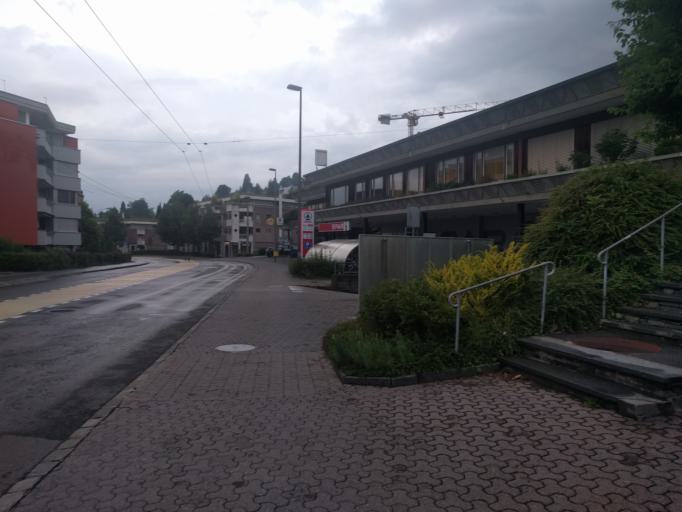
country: CH
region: Lucerne
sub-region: Lucerne-Land District
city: Adligenswil
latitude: 47.0548
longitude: 8.3442
